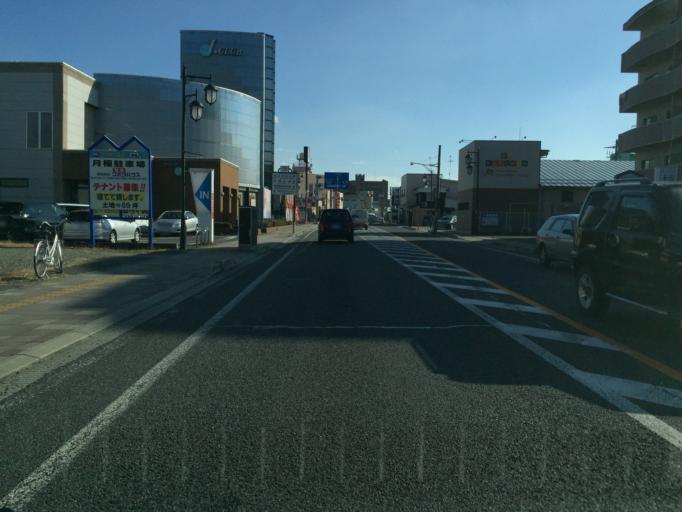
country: JP
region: Fukushima
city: Koriyama
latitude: 37.3938
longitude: 140.3550
